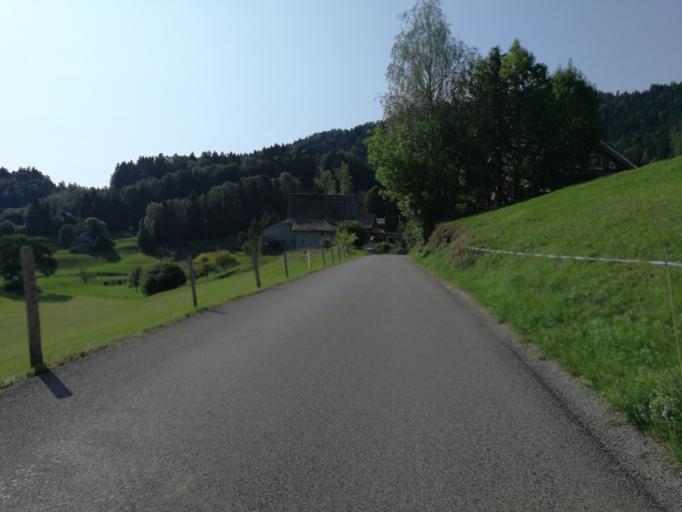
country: CH
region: Saint Gallen
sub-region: Wahlkreis Toggenburg
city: Krummenau
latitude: 47.2486
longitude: 9.1496
